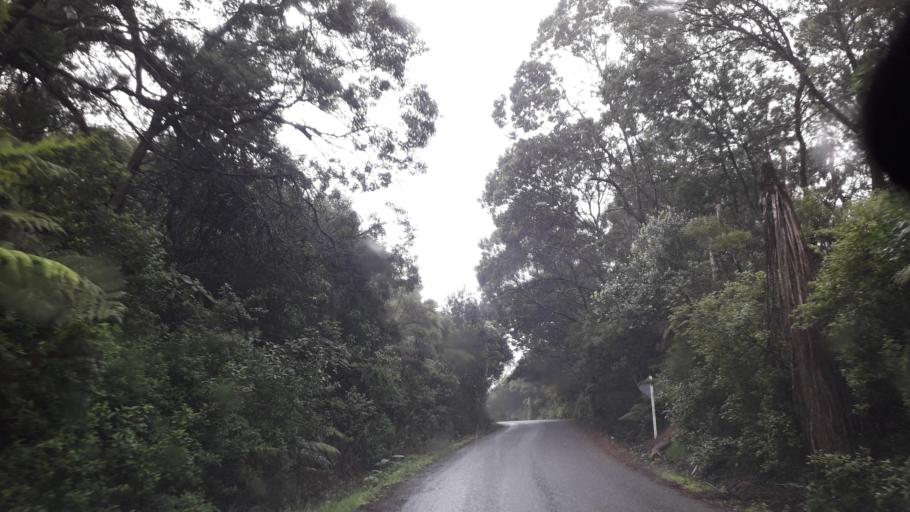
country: NZ
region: Northland
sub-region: Far North District
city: Paihia
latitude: -35.2313
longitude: 174.2607
